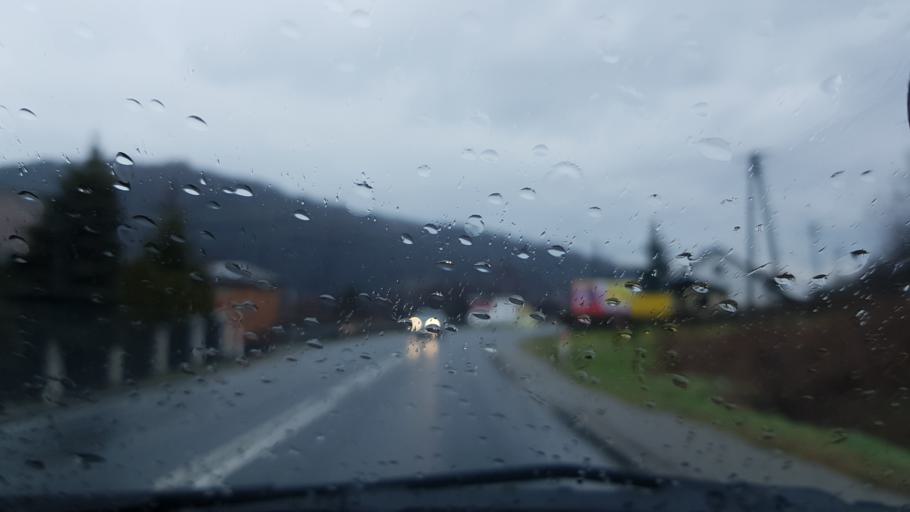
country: PL
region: Lesser Poland Voivodeship
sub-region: Powiat suski
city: Stryszawa
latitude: 49.7365
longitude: 19.5386
